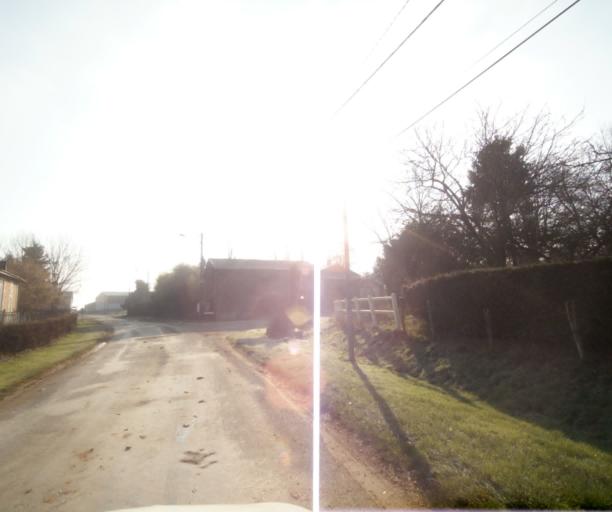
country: FR
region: Champagne-Ardenne
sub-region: Departement de la Haute-Marne
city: Montier-en-Der
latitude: 48.4965
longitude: 4.7236
